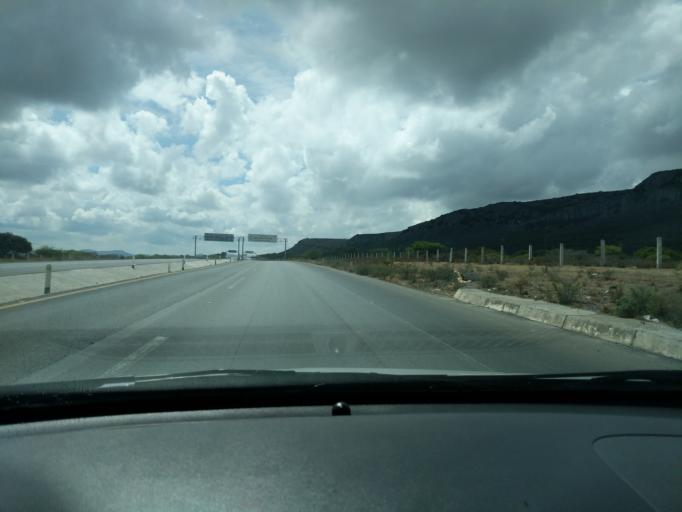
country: MX
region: Zacatecas
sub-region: Pinos
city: Santiago
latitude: 22.4021
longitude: -101.3811
